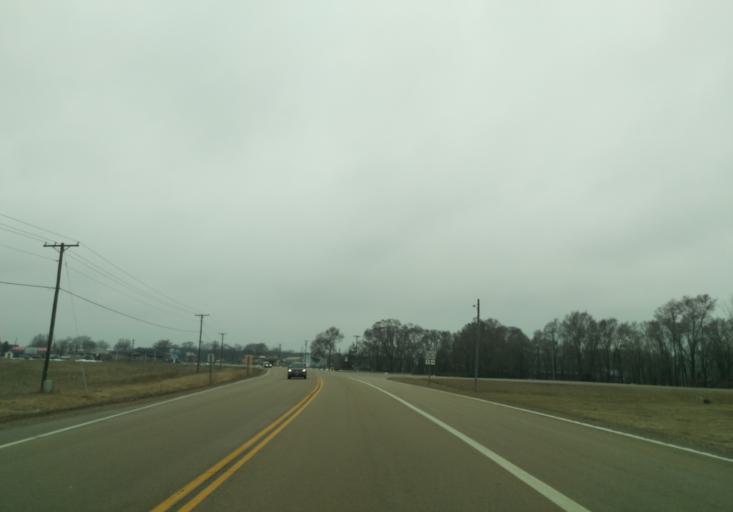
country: US
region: Wisconsin
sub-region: Sauk County
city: Spring Green
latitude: 43.1888
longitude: -90.0688
